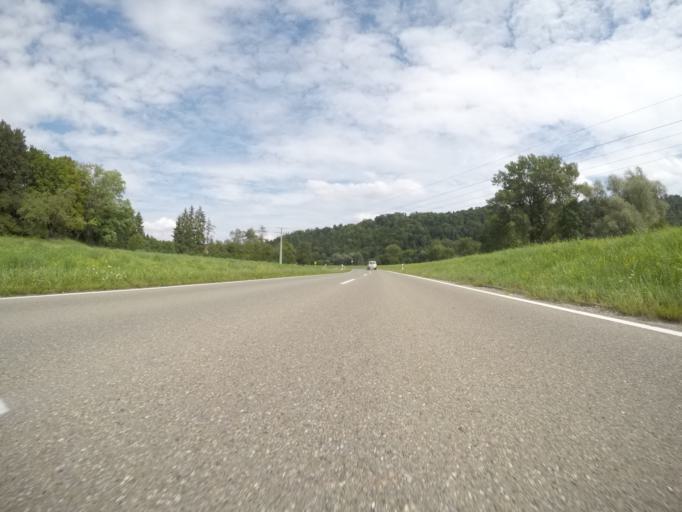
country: DE
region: Baden-Wuerttemberg
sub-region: Tuebingen Region
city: Hirrlingen
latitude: 48.4540
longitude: 8.8682
